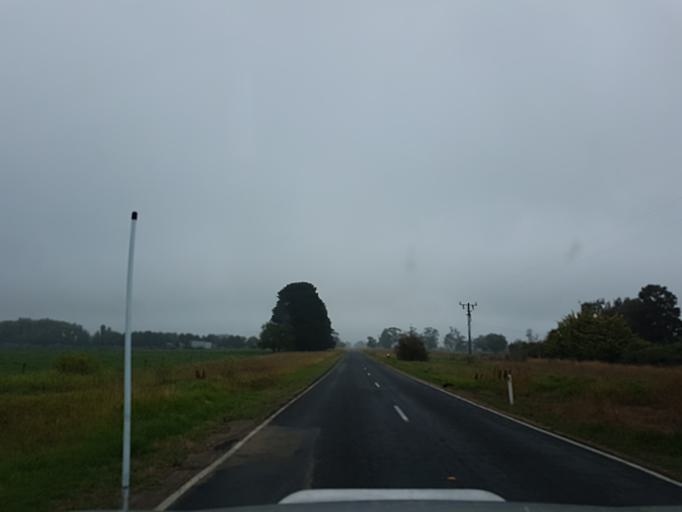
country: AU
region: Victoria
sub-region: Wellington
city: Sale
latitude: -38.0637
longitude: 147.0400
